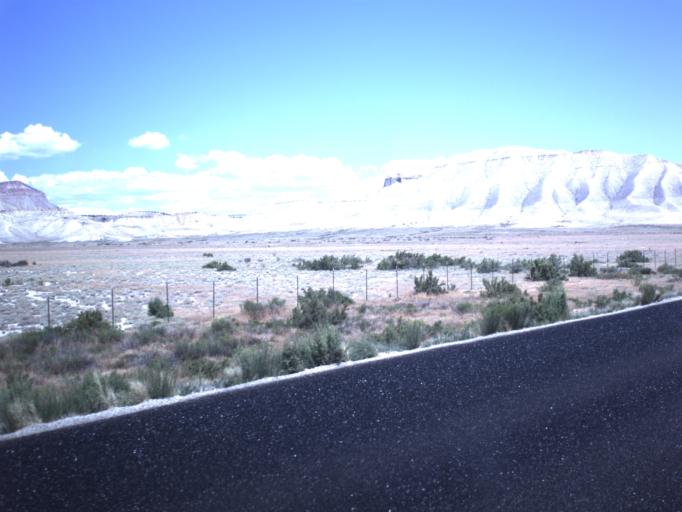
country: US
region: Utah
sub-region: Emery County
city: Ferron
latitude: 38.9932
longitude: -111.1670
